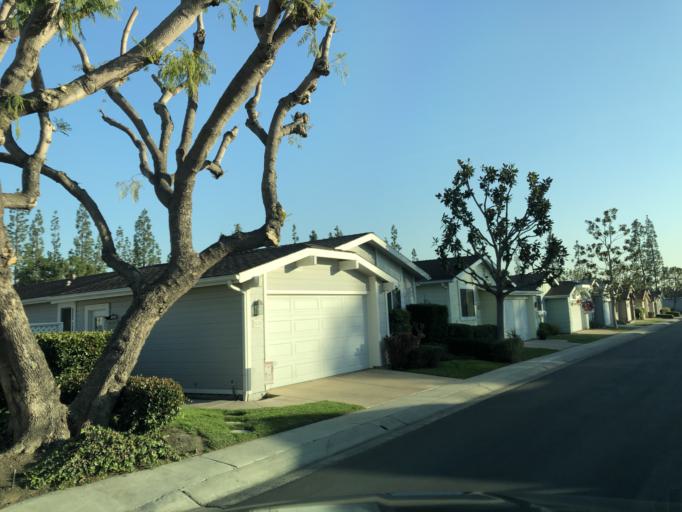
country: US
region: California
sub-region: Orange County
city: Orange
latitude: 33.7729
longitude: -117.8473
